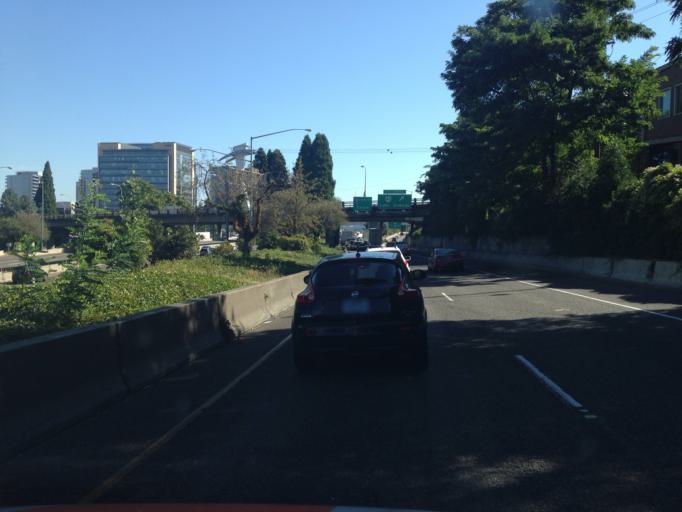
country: US
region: Oregon
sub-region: Multnomah County
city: Portland
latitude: 45.5027
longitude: -122.6745
